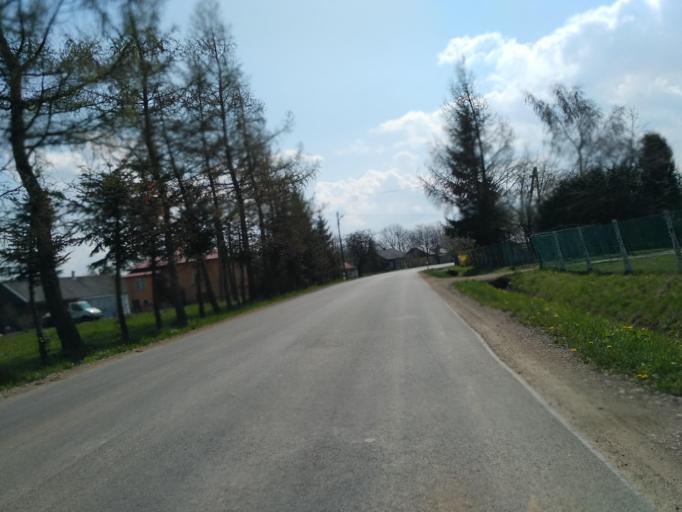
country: PL
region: Subcarpathian Voivodeship
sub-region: Powiat sanocki
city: Zarszyn
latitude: 49.5210
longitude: 21.9989
